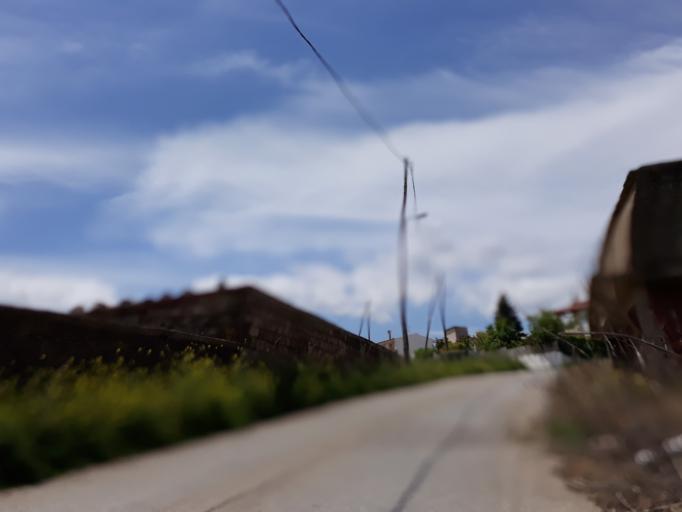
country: GR
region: Attica
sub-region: Nomarchia Dytikis Attikis
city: Magoula
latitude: 38.1760
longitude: 23.5481
